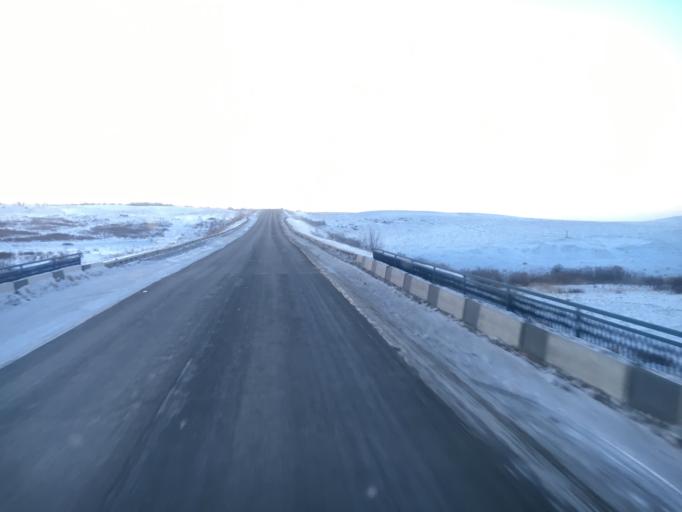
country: KZ
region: Aqtoebe
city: Aqtobe
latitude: 50.2830
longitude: 57.7619
